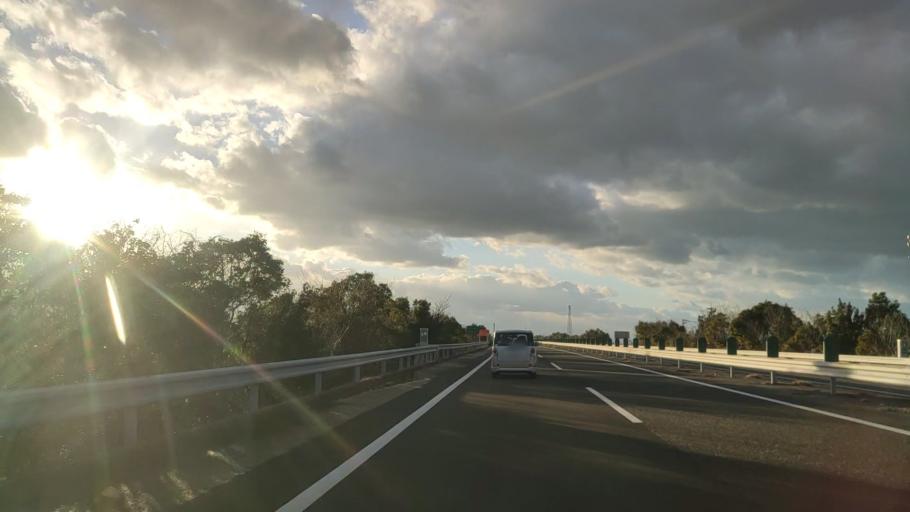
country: JP
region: Ehime
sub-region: Shikoku-chuo Shi
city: Matsuyama
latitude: 33.7859
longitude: 132.8672
